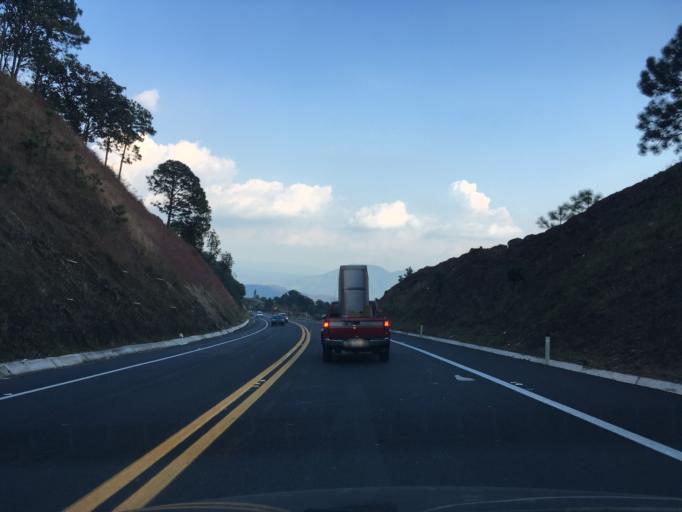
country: MX
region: Michoacan
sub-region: Uruapan
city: Toreo Bajo (El Toreo Bajo)
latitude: 19.4155
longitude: -101.9804
